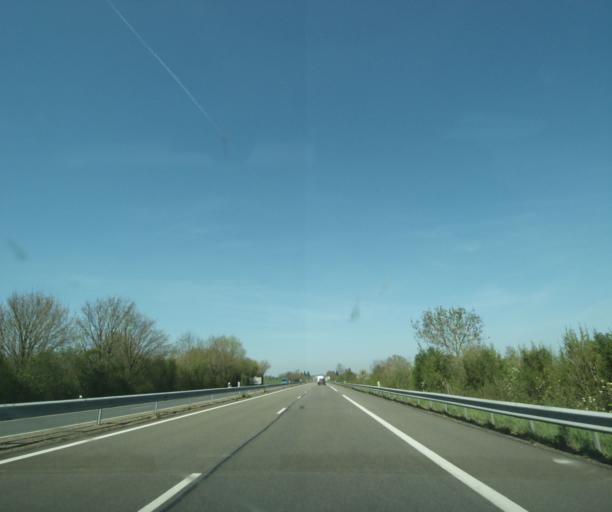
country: FR
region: Bourgogne
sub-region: Departement de la Nievre
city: La Charite-sur-Loire
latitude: 47.1763
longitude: 3.0442
